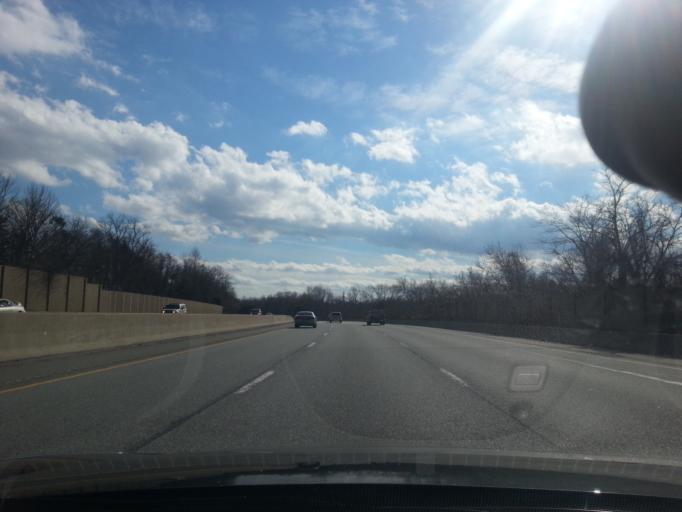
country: US
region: Pennsylvania
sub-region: Delaware County
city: Radnor
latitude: 40.0317
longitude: -75.3625
